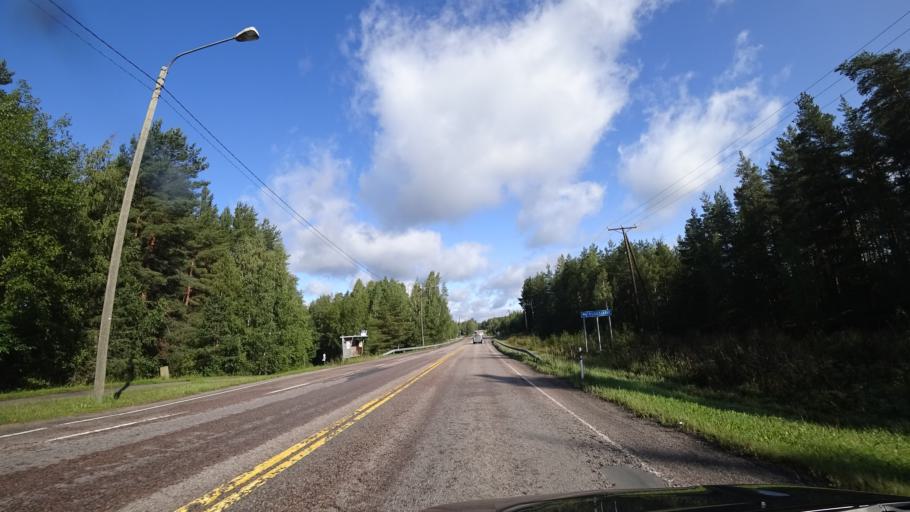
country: FI
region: Uusimaa
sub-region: Helsinki
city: Tuusula
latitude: 60.4165
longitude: 25.0009
